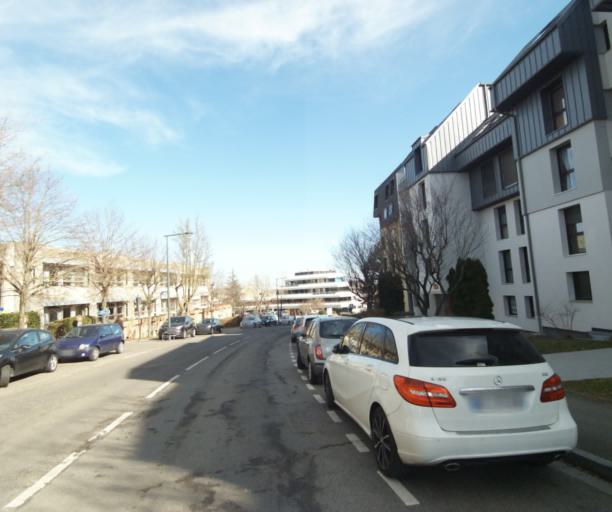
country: FR
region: Lorraine
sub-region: Departement de Meurthe-et-Moselle
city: Villers-les-Nancy
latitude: 48.6715
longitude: 6.1501
